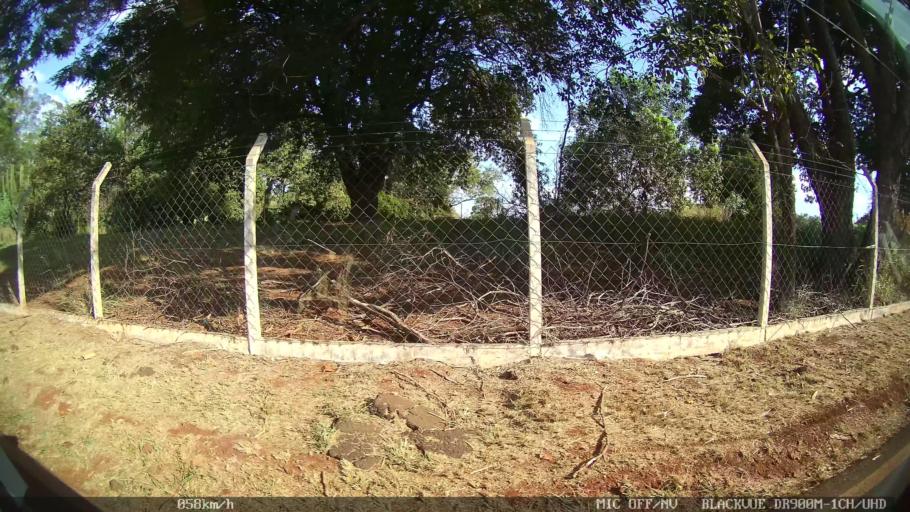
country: BR
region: Sao Paulo
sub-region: Ribeirao Preto
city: Ribeirao Preto
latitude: -21.1784
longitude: -47.8417
